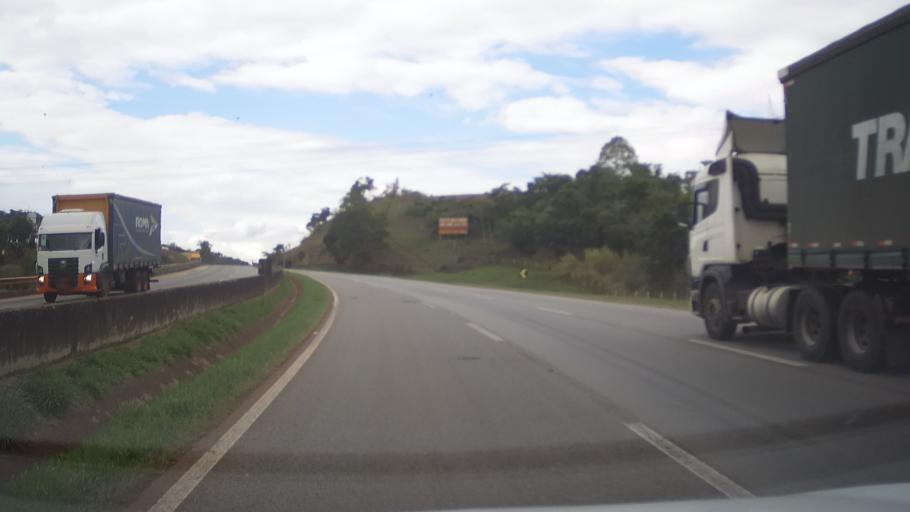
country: BR
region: Minas Gerais
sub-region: Igarape
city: Igarape
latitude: -20.2815
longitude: -44.4286
